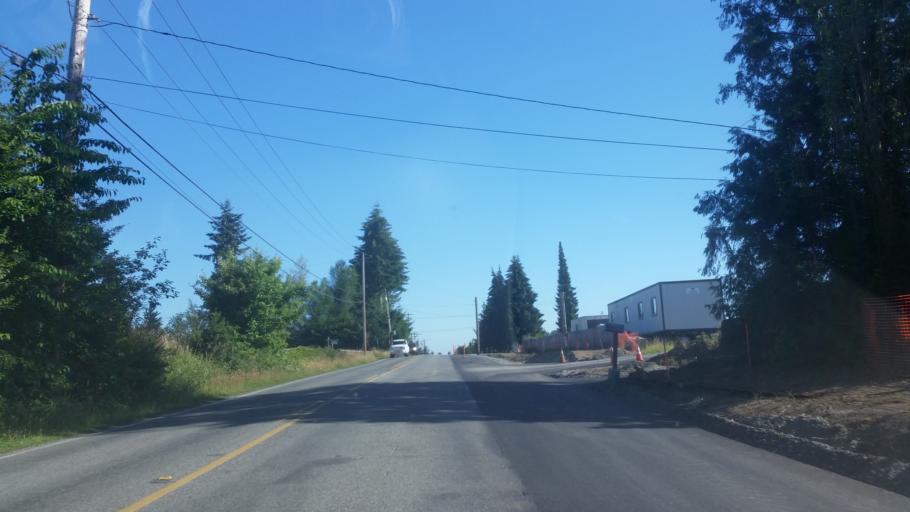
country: US
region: Washington
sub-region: Snohomish County
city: Maltby
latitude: 47.8170
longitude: -122.1100
